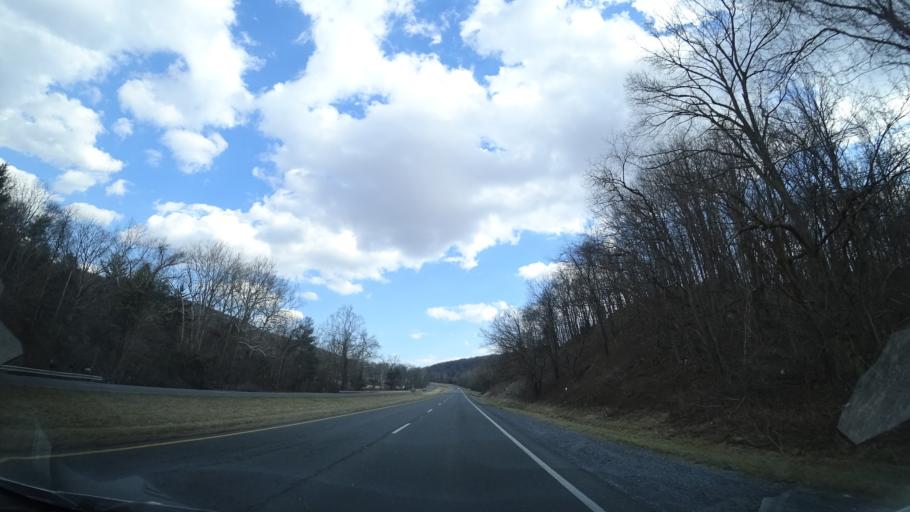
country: US
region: Virginia
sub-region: Warren County
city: Shenandoah Farms
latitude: 39.0258
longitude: -77.9766
